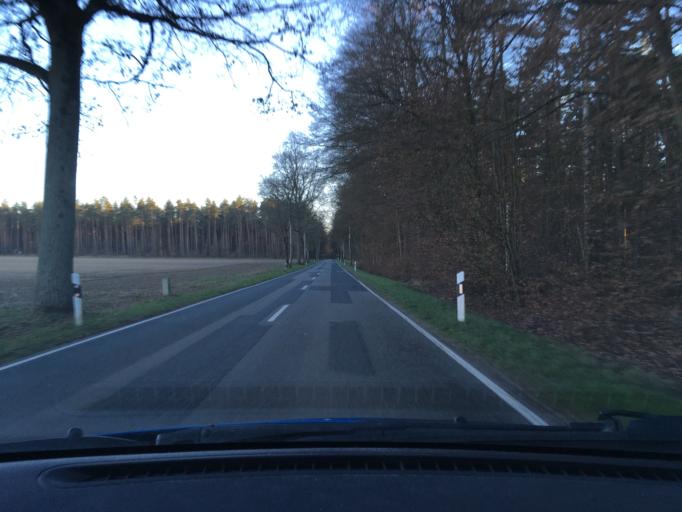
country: DE
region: Lower Saxony
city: Dahlem
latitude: 53.2436
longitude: 10.7491
